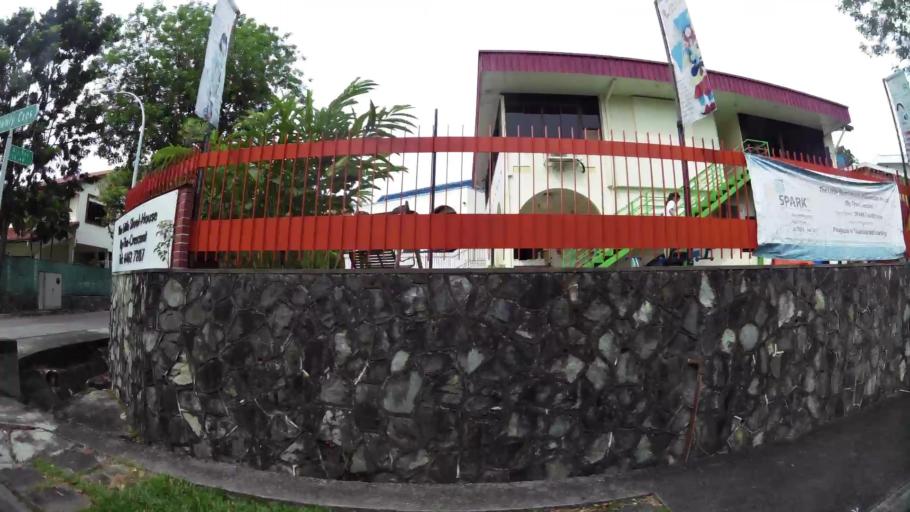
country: SG
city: Singapore
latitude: 1.3269
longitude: 103.7945
